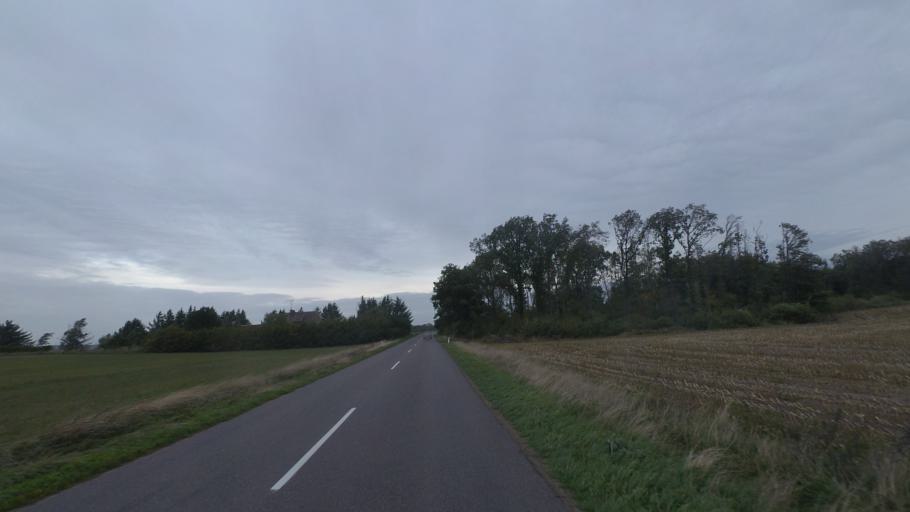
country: DK
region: Capital Region
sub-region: Bornholm Kommune
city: Nexo
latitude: 55.0186
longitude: 15.0965
